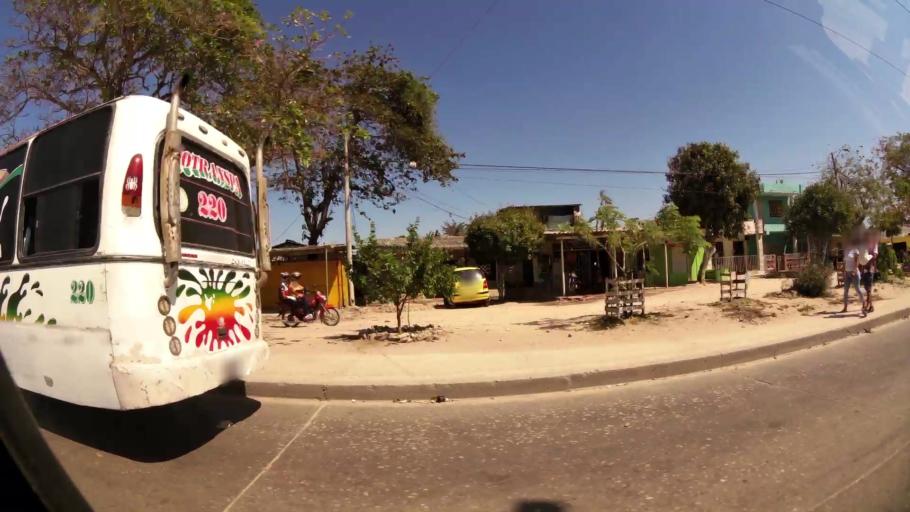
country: CO
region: Atlantico
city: Barranquilla
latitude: 10.9525
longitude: -74.7738
